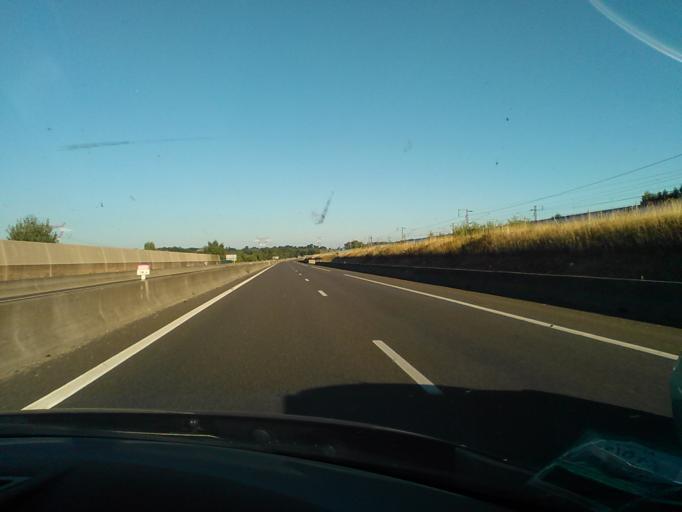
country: FR
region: Rhone-Alpes
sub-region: Departement du Rhone
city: Jonage
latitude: 45.8163
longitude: 5.0508
